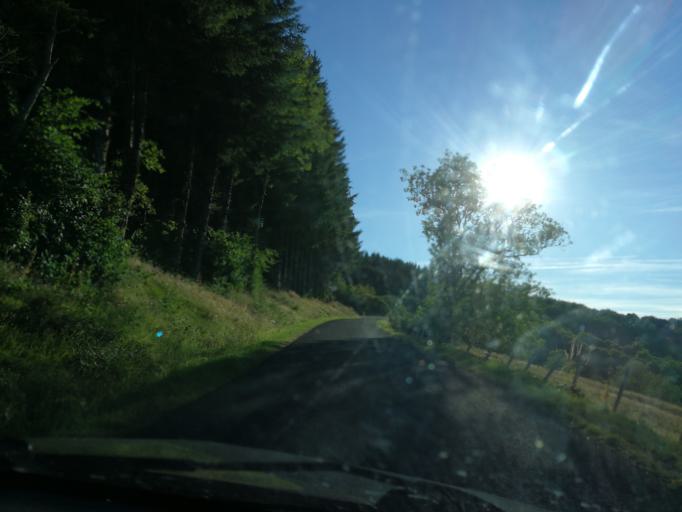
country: FR
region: Auvergne
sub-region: Departement du Cantal
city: Vic-sur-Cere
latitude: 45.0783
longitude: 2.5655
